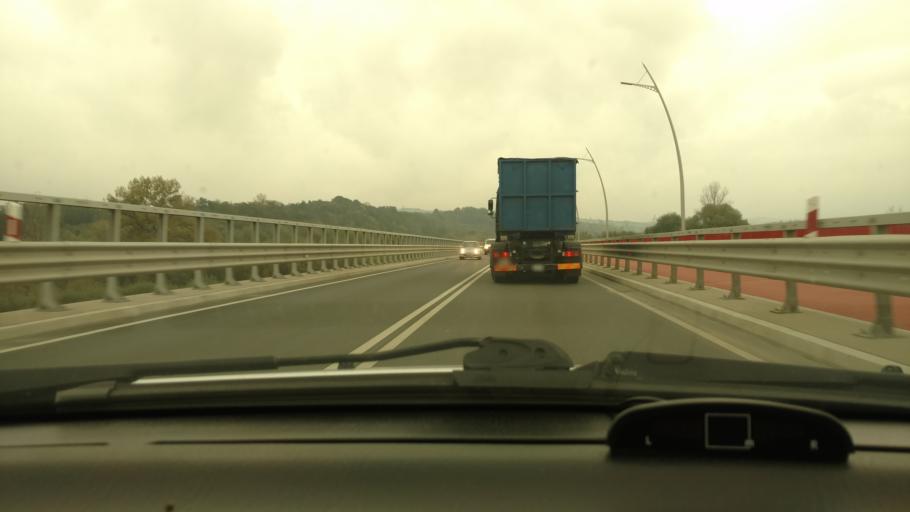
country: PL
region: Lesser Poland Voivodeship
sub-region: Powiat nowosadecki
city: Chelmiec
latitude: 49.6411
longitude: 20.6820
